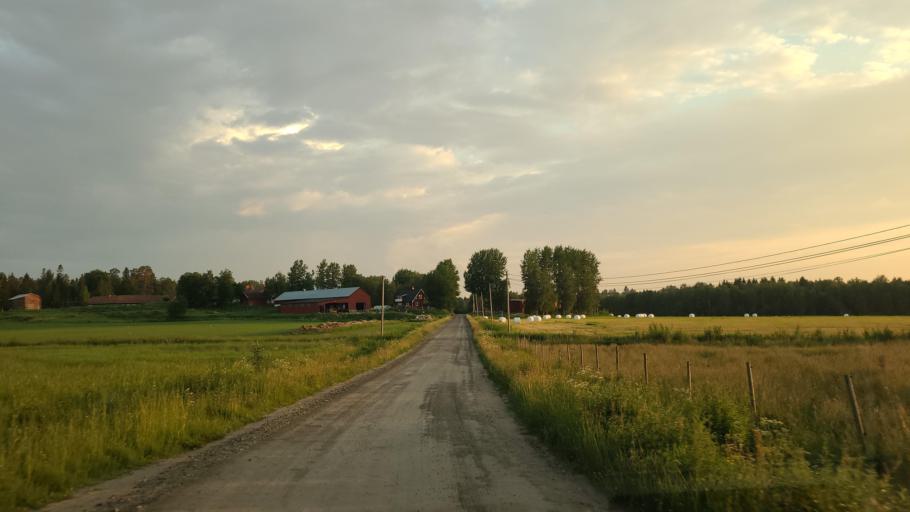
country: SE
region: Vaesterbotten
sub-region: Robertsfors Kommun
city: Robertsfors
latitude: 64.0656
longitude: 20.8705
